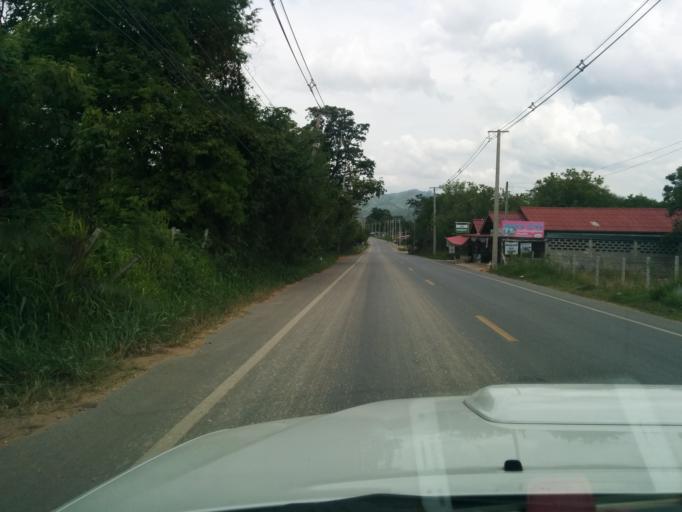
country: TH
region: Sara Buri
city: Muak Lek
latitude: 14.6087
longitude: 101.2125
